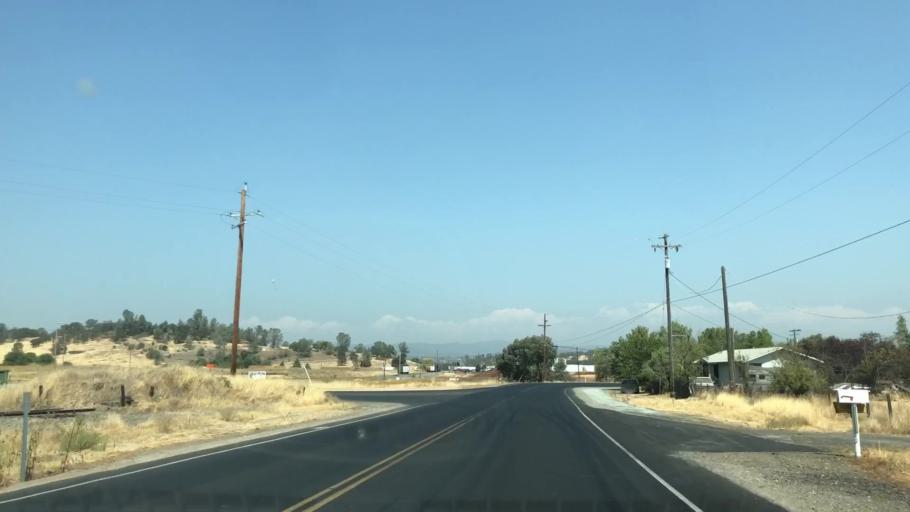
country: US
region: California
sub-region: Tuolumne County
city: Jamestown
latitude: 37.8792
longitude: -120.4578
